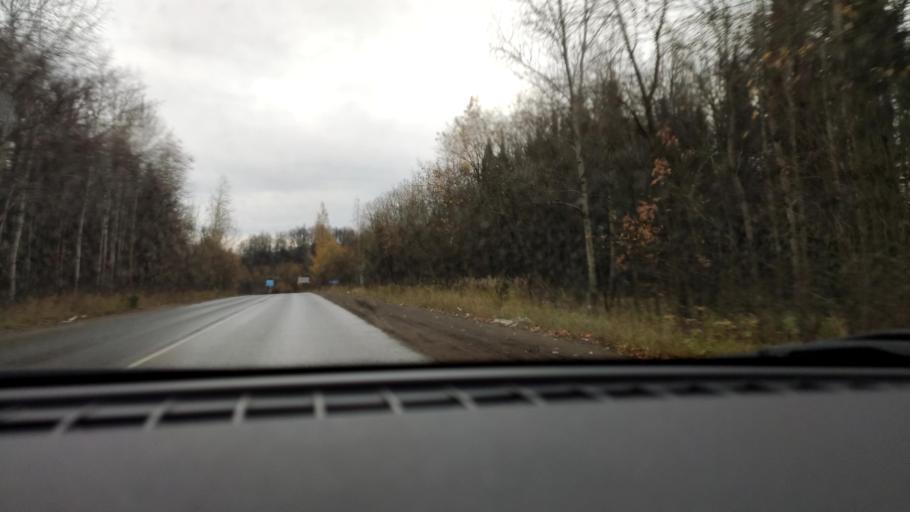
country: RU
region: Perm
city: Froly
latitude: 57.9555
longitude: 56.2985
